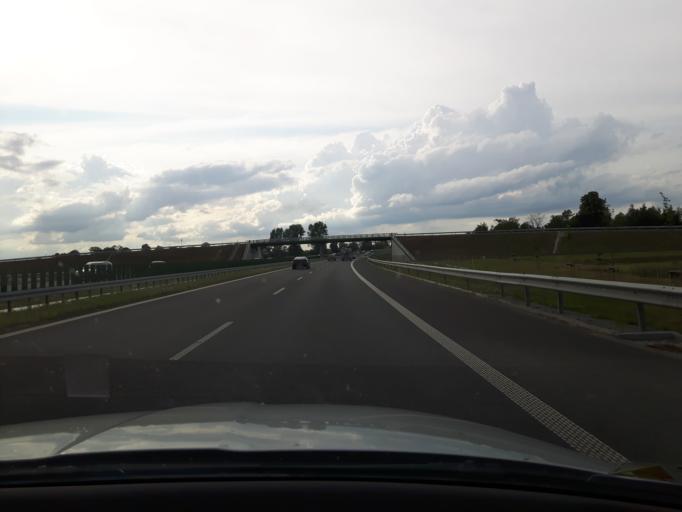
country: PL
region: Pomeranian Voivodeship
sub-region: Powiat nowodworski
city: Nowy Dwor Gdanski
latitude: 54.1754
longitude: 19.1919
